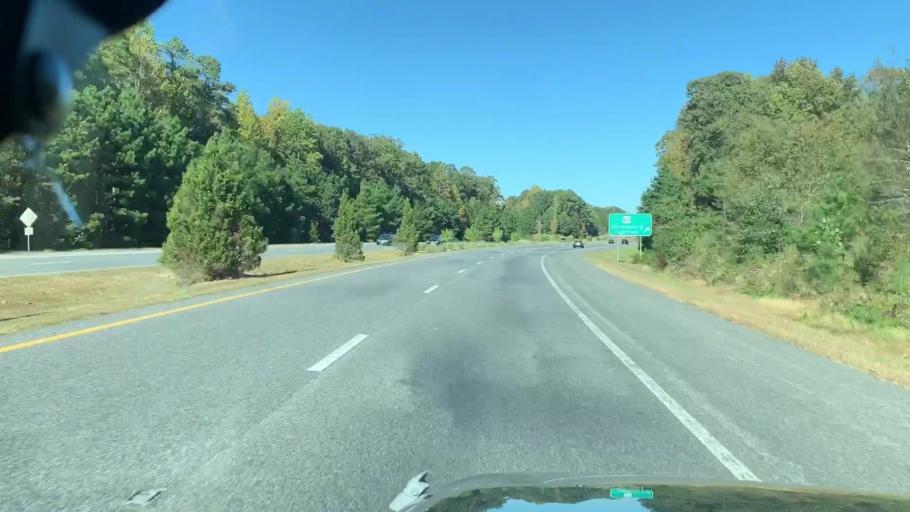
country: US
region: Virginia
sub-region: James City County
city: Williamsburg
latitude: 37.3315
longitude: -76.7548
